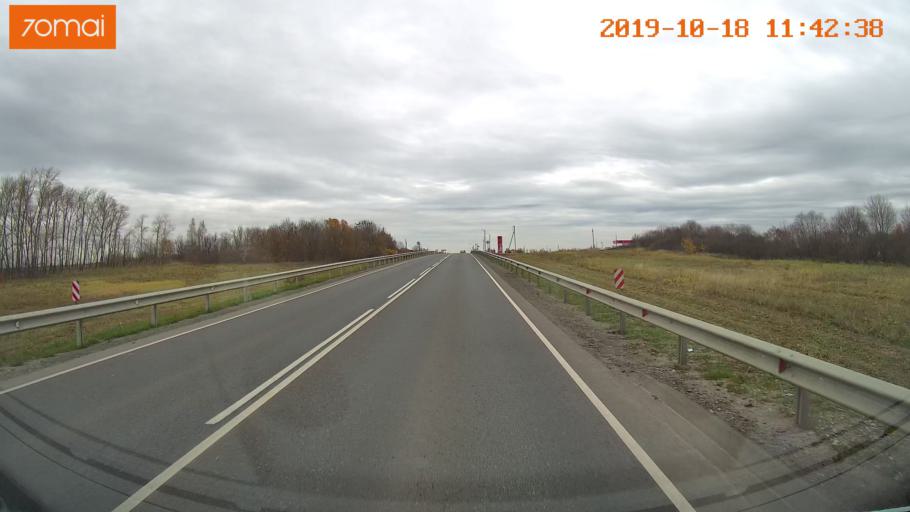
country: RU
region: Rjazan
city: Oktyabr'skiy
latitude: 54.1903
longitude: 38.9317
